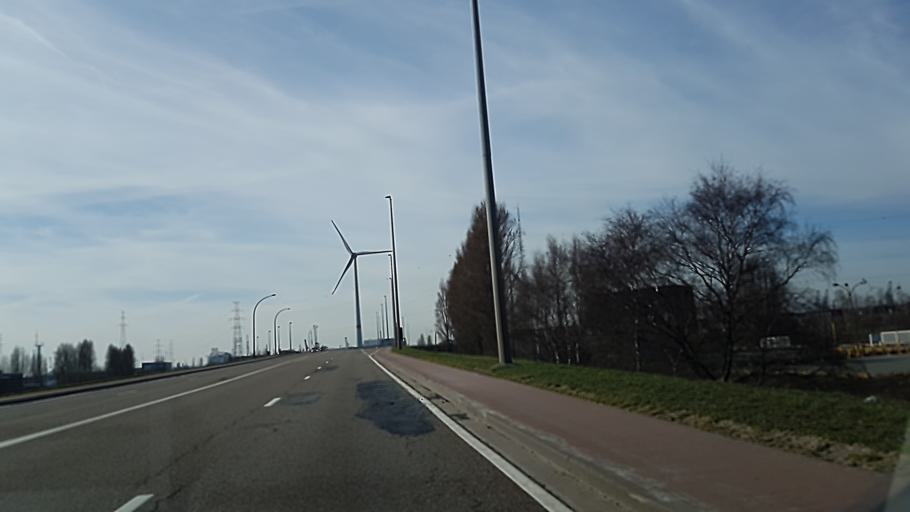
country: BE
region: Flanders
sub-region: Provincie Antwerpen
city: Antwerpen
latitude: 51.2653
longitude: 4.3862
